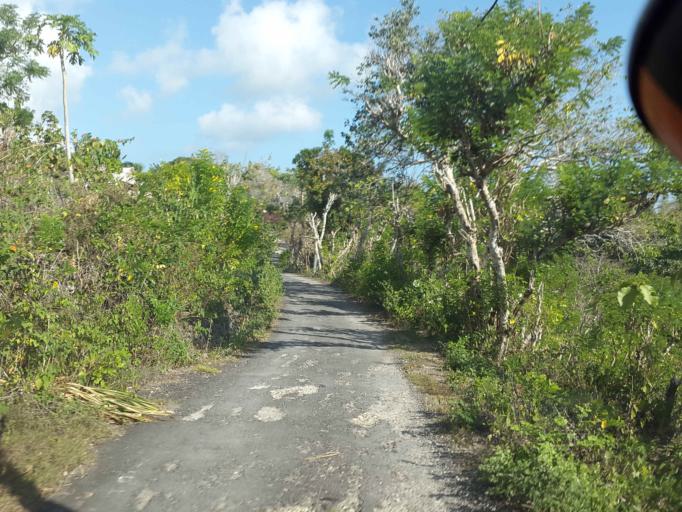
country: ID
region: Bali
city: Pondokkaha Kelod
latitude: -8.7389
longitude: 115.4829
